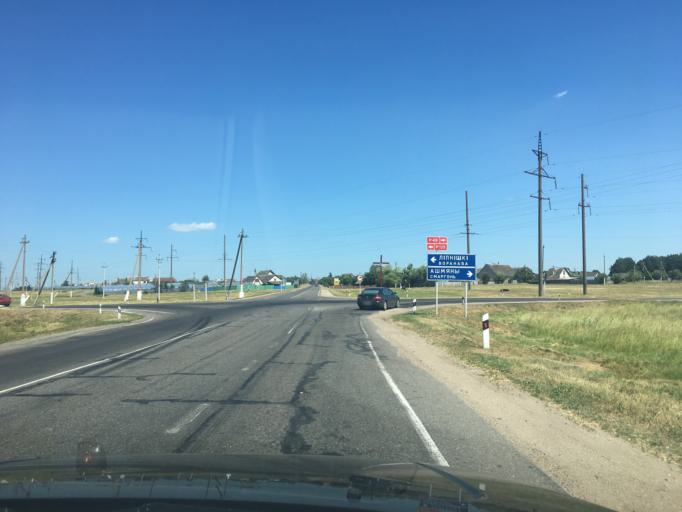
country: BY
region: Grodnenskaya
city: Iwye
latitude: 53.9148
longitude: 25.7661
